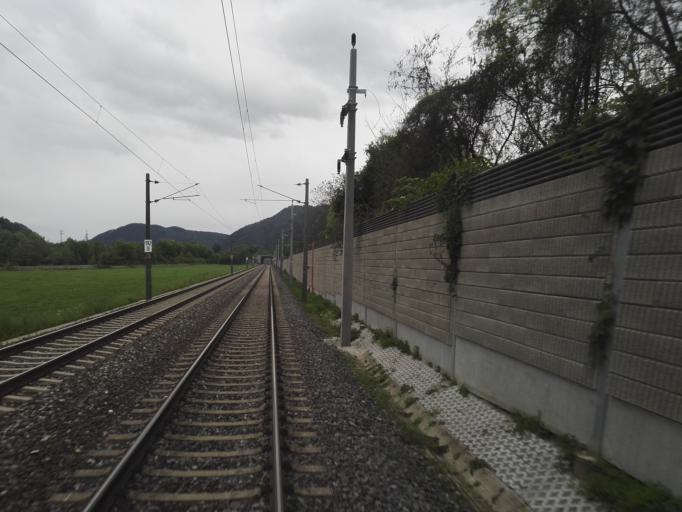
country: AT
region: Styria
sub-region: Politischer Bezirk Graz-Umgebung
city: Deutschfeistritz
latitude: 47.1899
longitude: 15.3349
